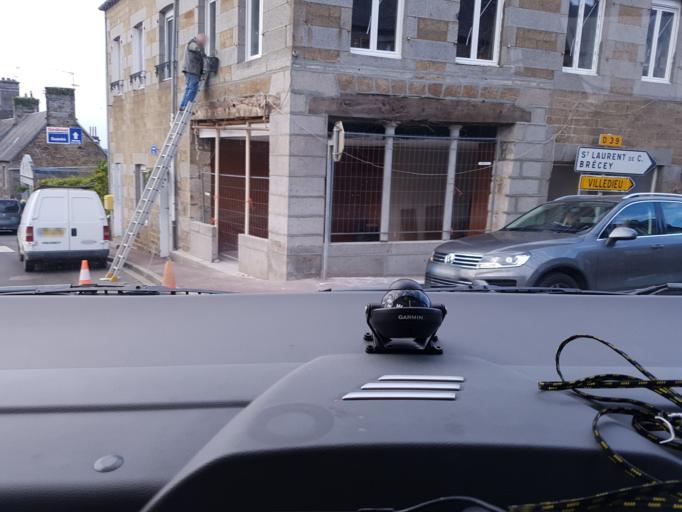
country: FR
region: Lower Normandy
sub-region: Departement du Calvados
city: Saint-Sever-Calvados
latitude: 48.7504
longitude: -1.0664
